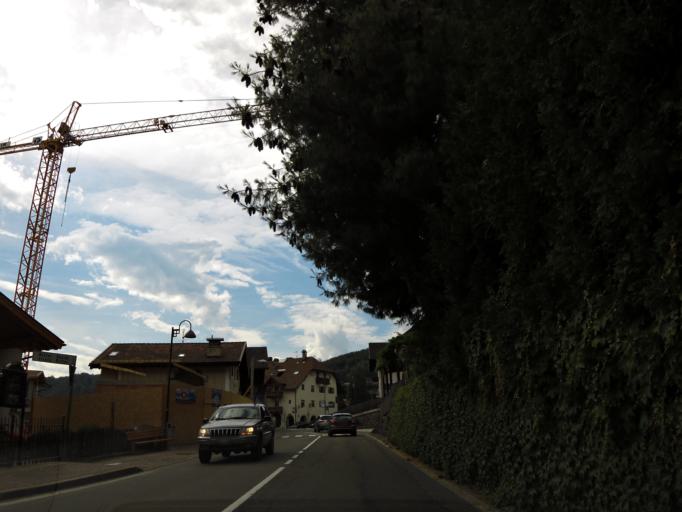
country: IT
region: Trentino-Alto Adige
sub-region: Bolzano
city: Siusi
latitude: 46.5454
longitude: 11.5619
